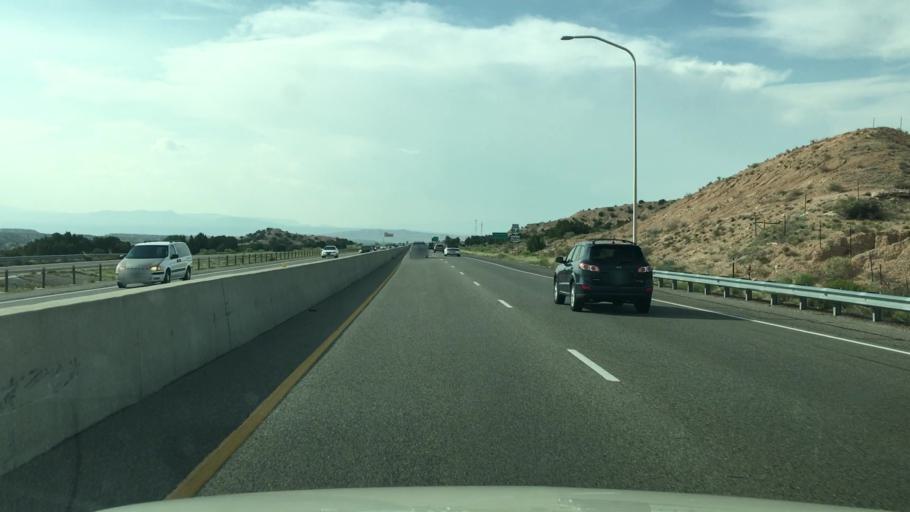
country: US
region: New Mexico
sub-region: Santa Fe County
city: Nambe
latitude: 35.8272
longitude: -105.9794
